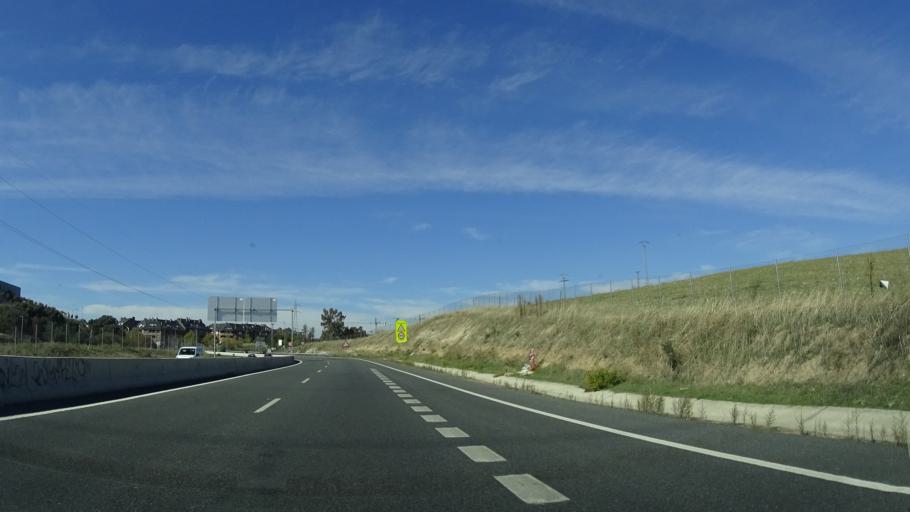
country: ES
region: Madrid
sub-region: Provincia de Madrid
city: Villanueva del Pardillo
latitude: 40.4906
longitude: -3.9532
